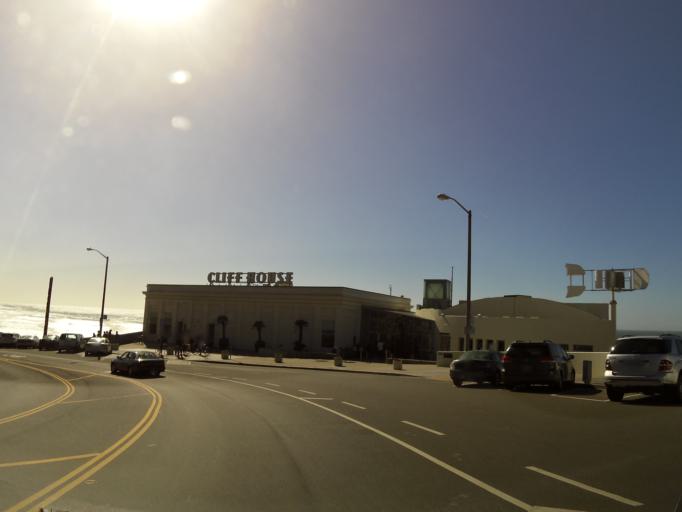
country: US
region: California
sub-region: Marin County
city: Sausalito
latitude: 37.7789
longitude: -122.5136
